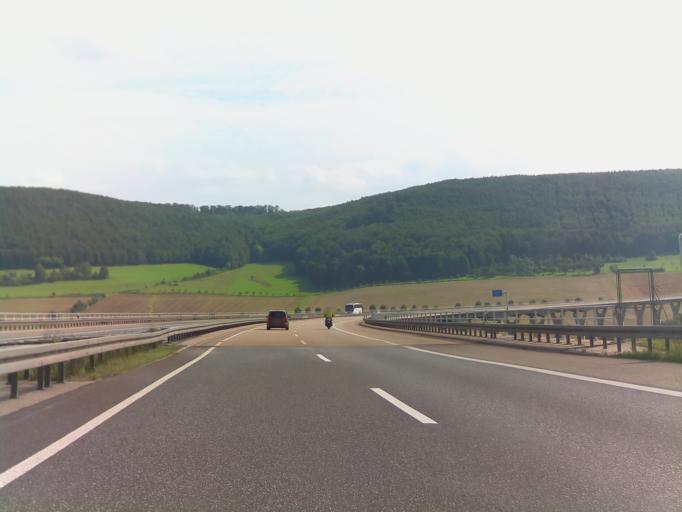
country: DE
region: Thuringia
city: Einhausen
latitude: 50.5334
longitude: 10.4766
